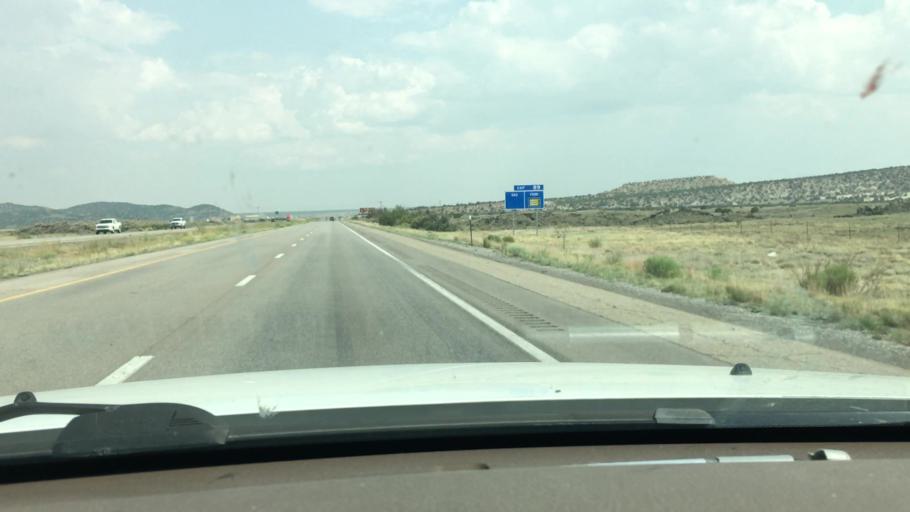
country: US
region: New Mexico
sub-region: Cibola County
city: Grants
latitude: 35.0927
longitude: -107.7822
